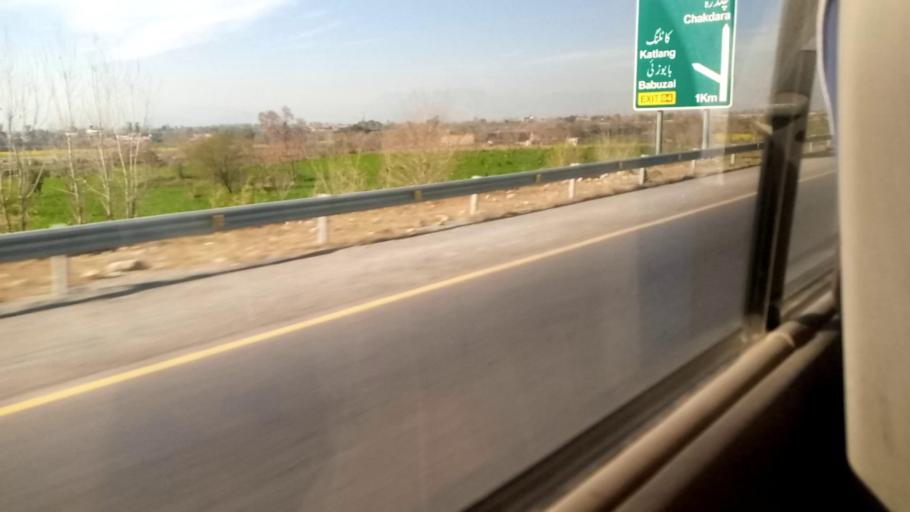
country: PK
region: Khyber Pakhtunkhwa
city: Mardan
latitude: 34.4091
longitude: 72.1298
